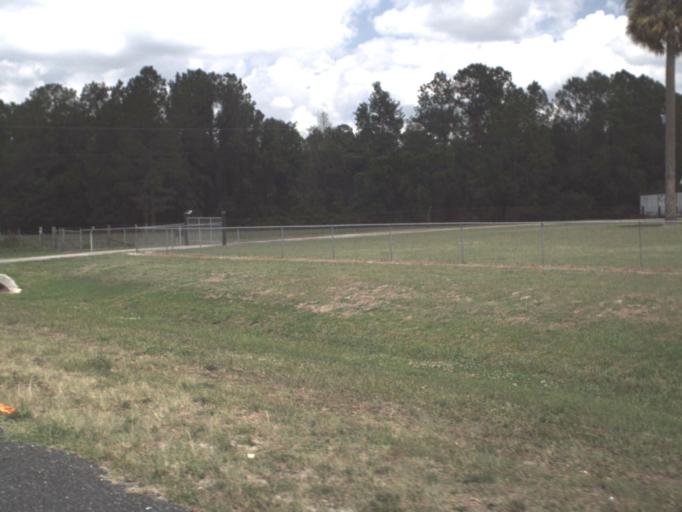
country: US
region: Florida
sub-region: Sumter County
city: Wildwood
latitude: 28.8567
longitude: -82.0709
